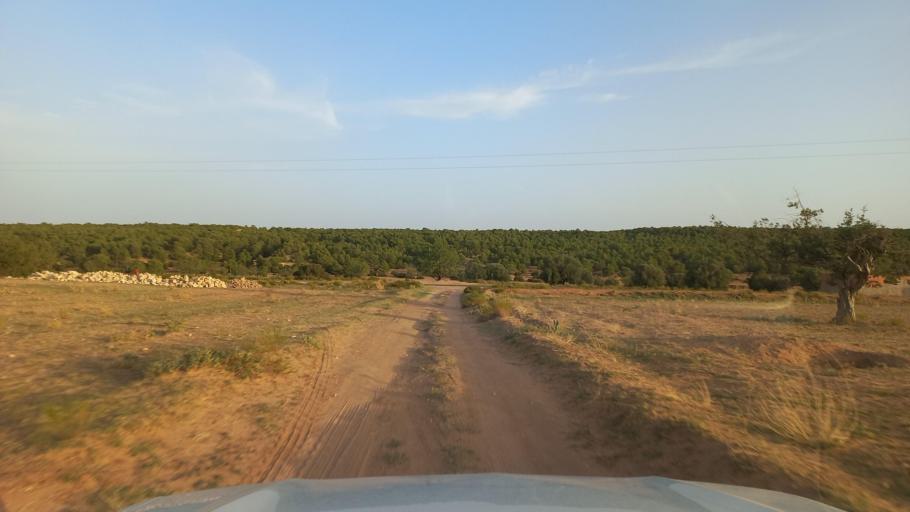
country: TN
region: Al Qasrayn
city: Sbiba
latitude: 35.4095
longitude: 8.9146
